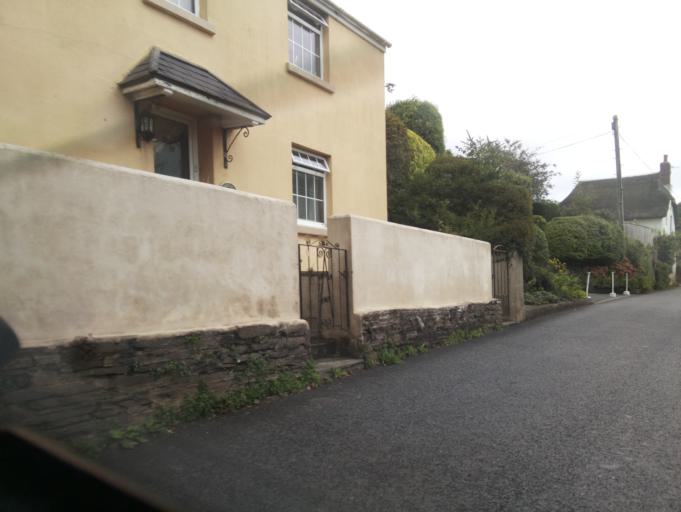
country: GB
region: England
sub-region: Devon
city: Salcombe
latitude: 50.2732
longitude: -3.6903
